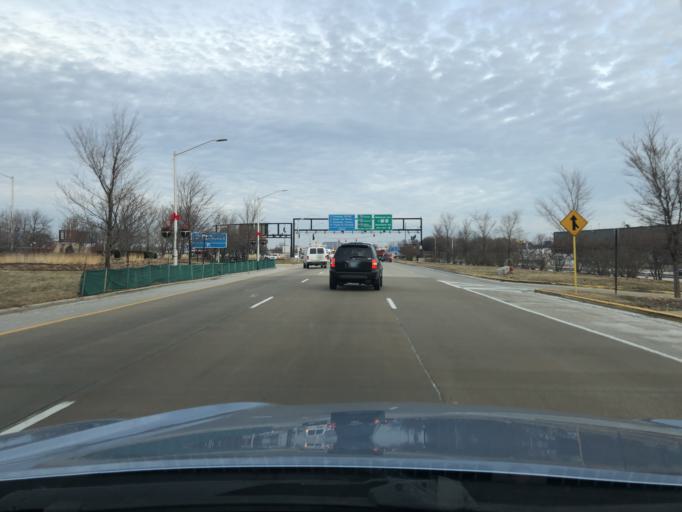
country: US
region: Illinois
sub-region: Cook County
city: Rosemont
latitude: 41.9750
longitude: -87.8861
